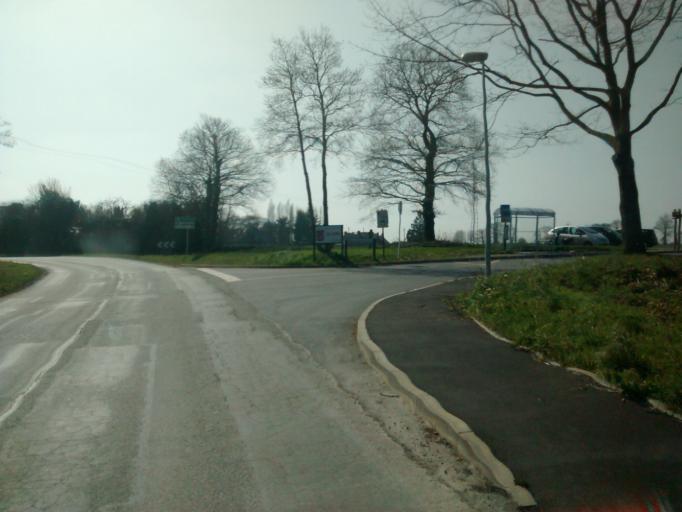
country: FR
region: Brittany
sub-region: Departement d'Ille-et-Vilaine
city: Monterfil
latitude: 48.0294
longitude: -2.0125
